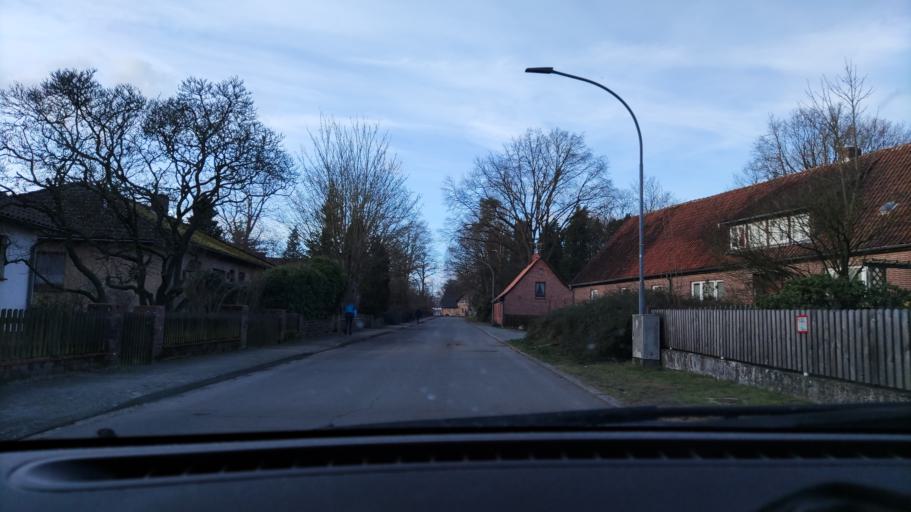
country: DE
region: Lower Saxony
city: Wriedel
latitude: 53.0313
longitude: 10.3039
